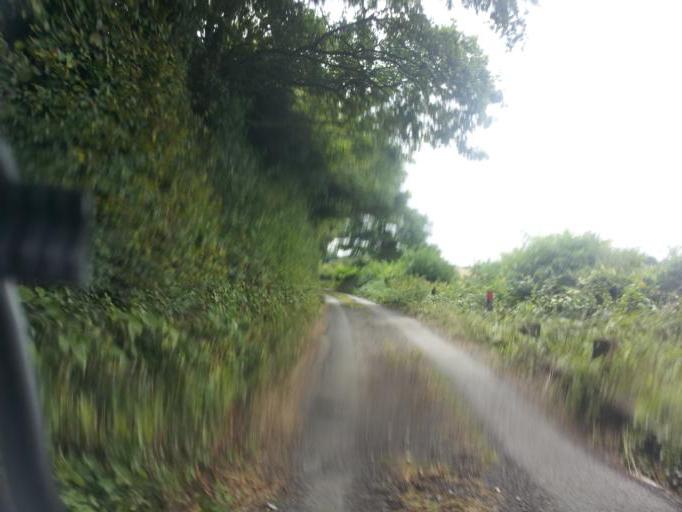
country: GB
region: England
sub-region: Kent
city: Newington
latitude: 51.3080
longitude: 0.6515
